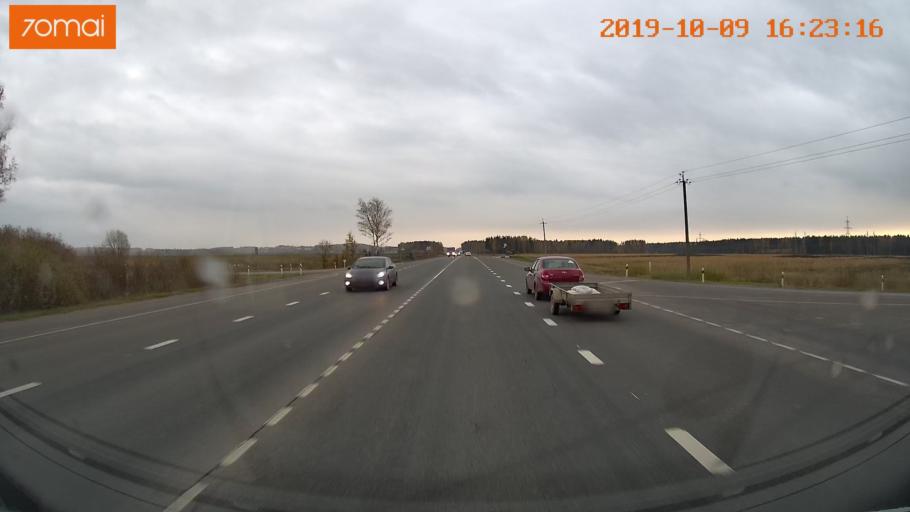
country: RU
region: Kostroma
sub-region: Kostromskoy Rayon
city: Kostroma
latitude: 57.6664
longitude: 40.8974
